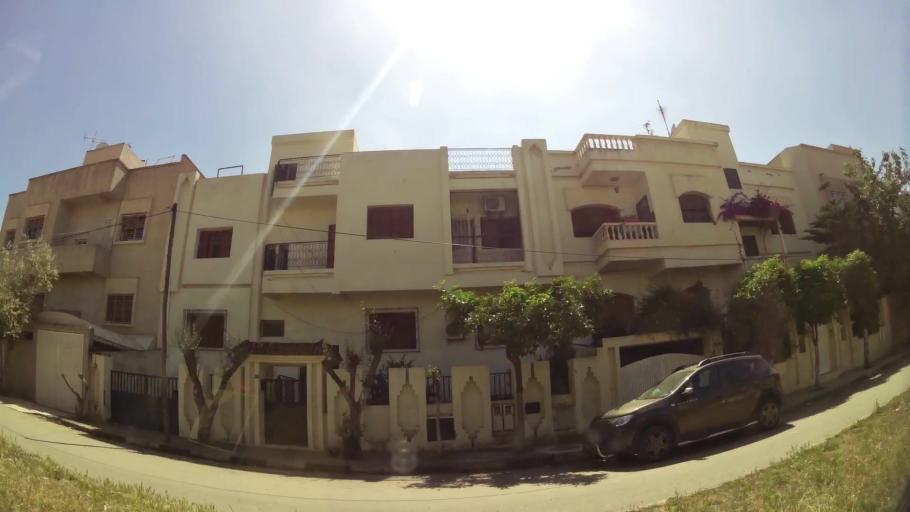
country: MA
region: Fes-Boulemane
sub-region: Fes
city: Fes
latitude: 34.0184
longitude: -5.0249
